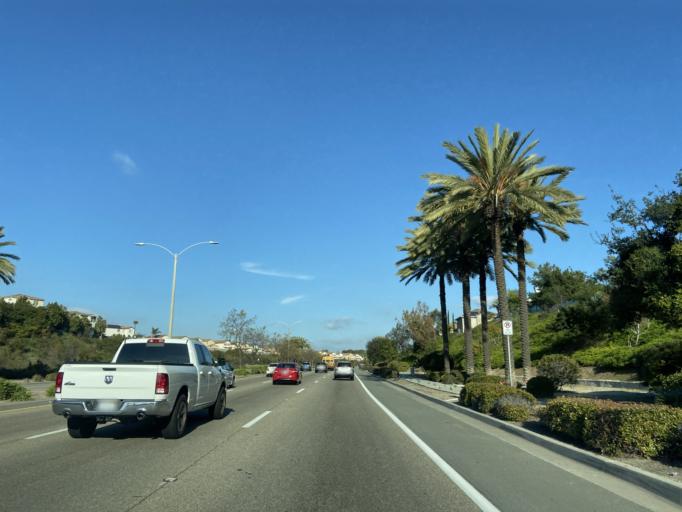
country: US
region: California
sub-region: San Diego County
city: Bonita
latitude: 32.6304
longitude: -116.9779
